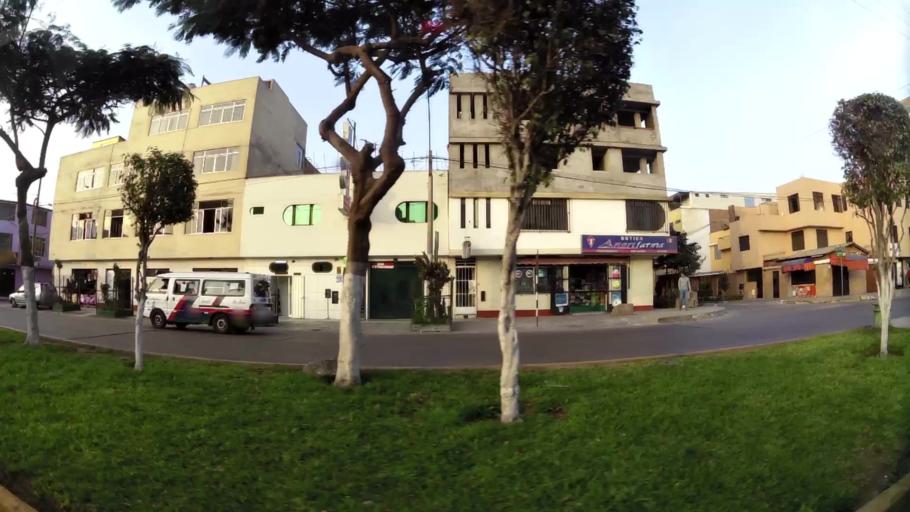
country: PE
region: Callao
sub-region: Callao
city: Callao
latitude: -12.0099
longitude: -77.1016
